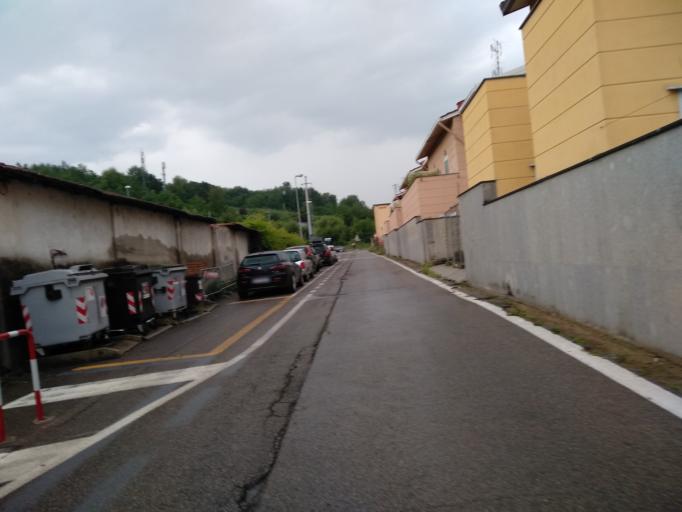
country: IT
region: Tuscany
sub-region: Province of Arezzo
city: San Giovanni Valdarno
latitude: 43.5620
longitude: 11.5289
